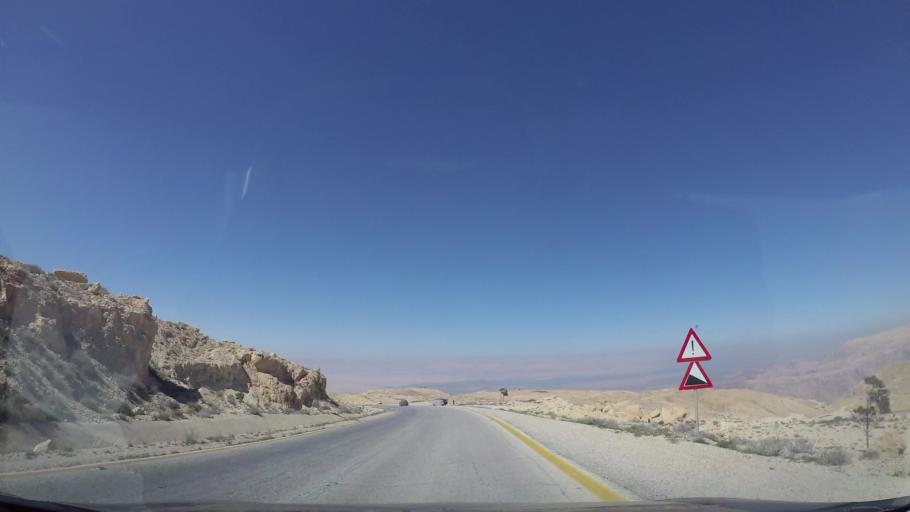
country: JO
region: Tafielah
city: At Tafilah
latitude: 30.8599
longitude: 35.5394
